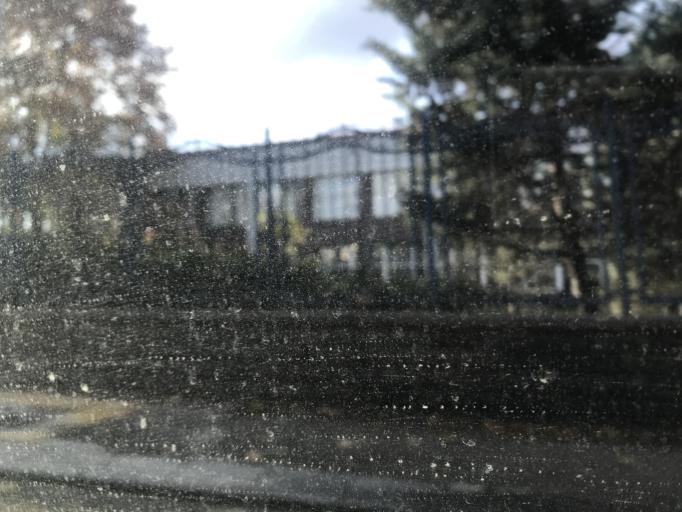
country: TR
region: Ankara
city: Ankara
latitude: 39.9601
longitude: 32.8664
